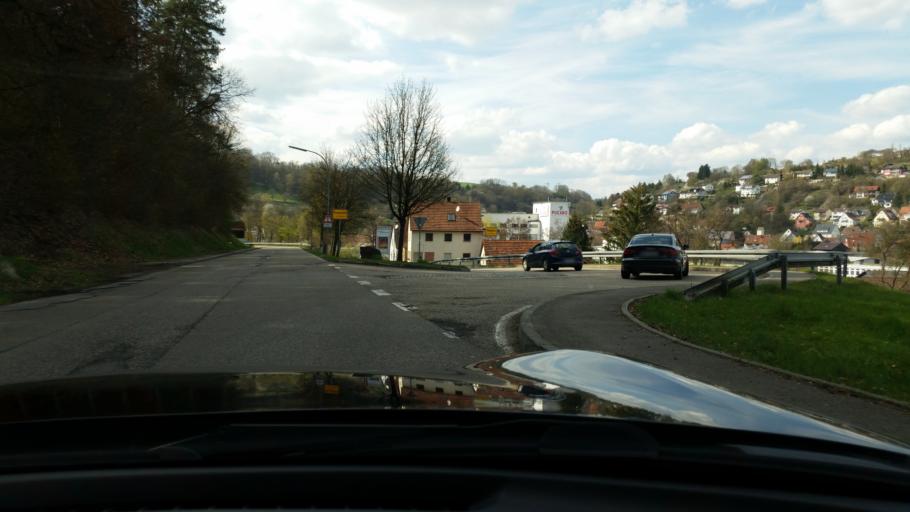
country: DE
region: Baden-Wuerttemberg
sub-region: Regierungsbezirk Stuttgart
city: Roigheim
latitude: 49.3617
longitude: 9.3468
